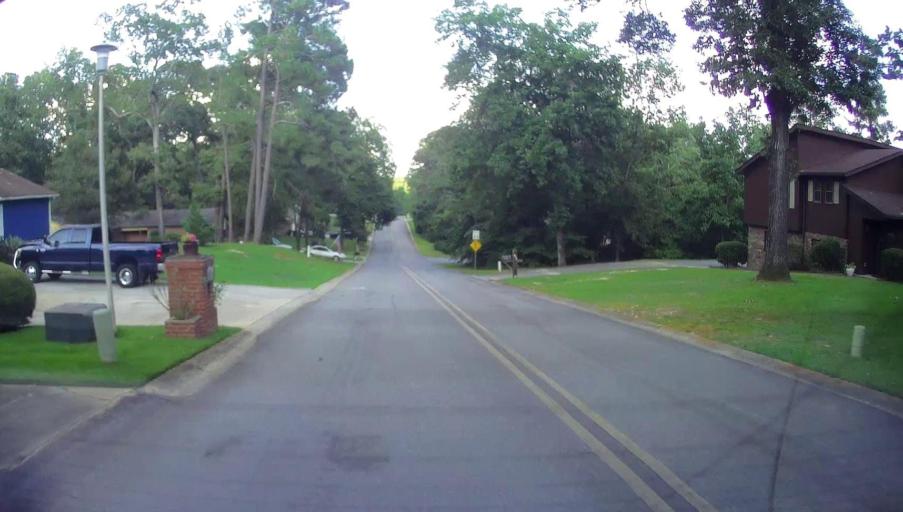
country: US
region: Georgia
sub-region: Houston County
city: Centerville
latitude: 32.5853
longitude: -83.6517
